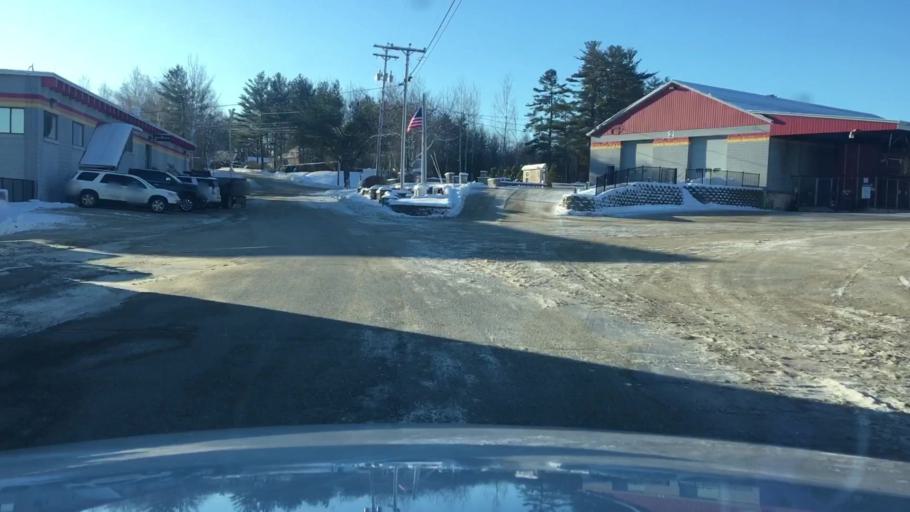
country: US
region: Maine
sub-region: Kennebec County
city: Belgrade
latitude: 44.4257
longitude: -69.8316
